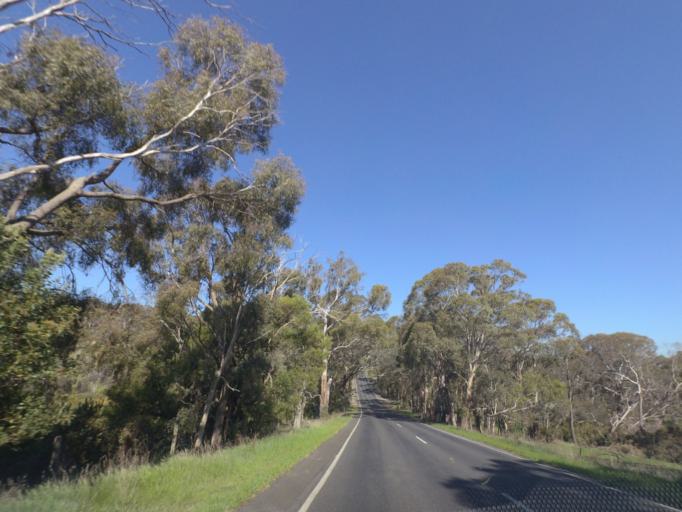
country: AU
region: Victoria
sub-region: Whittlesea
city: Whittlesea
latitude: -37.3409
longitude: 144.9906
